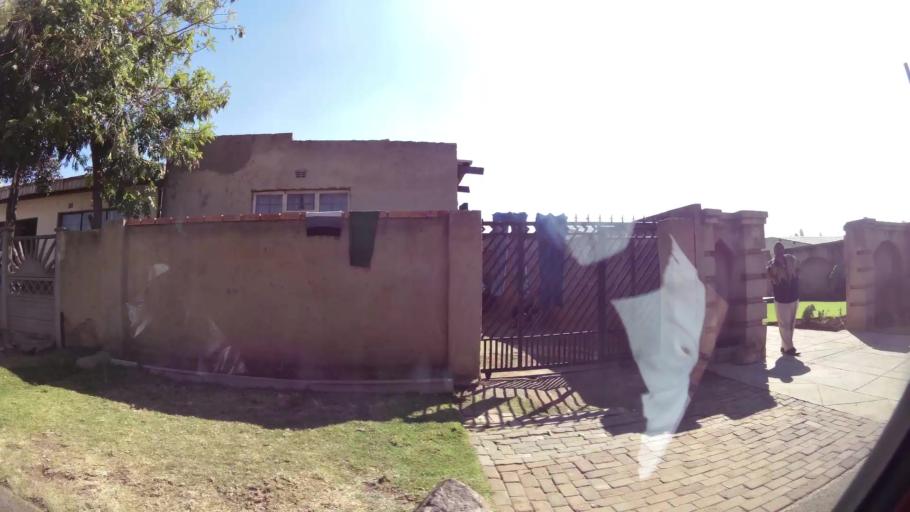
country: ZA
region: Gauteng
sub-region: City of Johannesburg Metropolitan Municipality
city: Soweto
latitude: -26.2310
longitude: 27.8840
